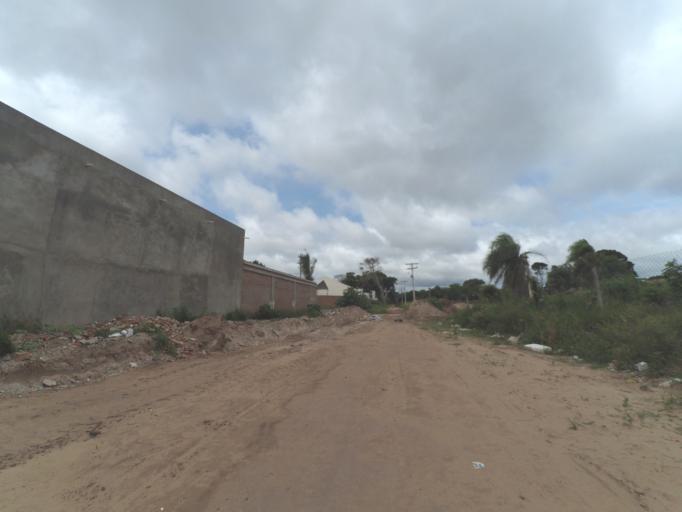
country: BO
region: Santa Cruz
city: Santa Cruz de la Sierra
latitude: -17.8175
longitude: -63.2352
